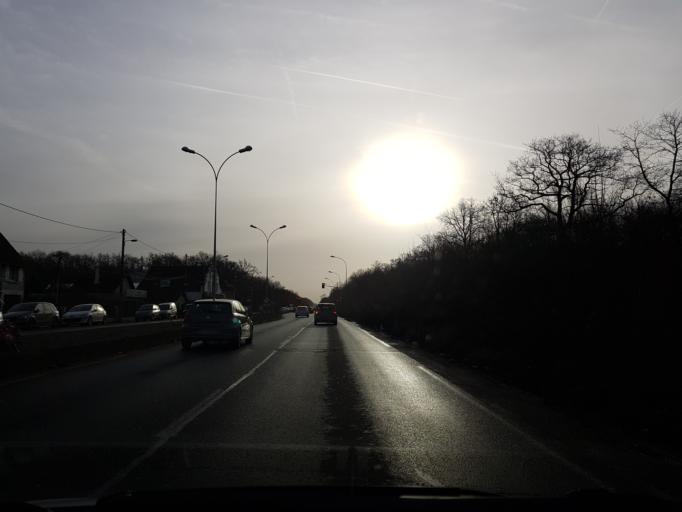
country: FR
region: Ile-de-France
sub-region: Departement de l'Essonne
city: Brunoy
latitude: 48.6793
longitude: 2.4950
